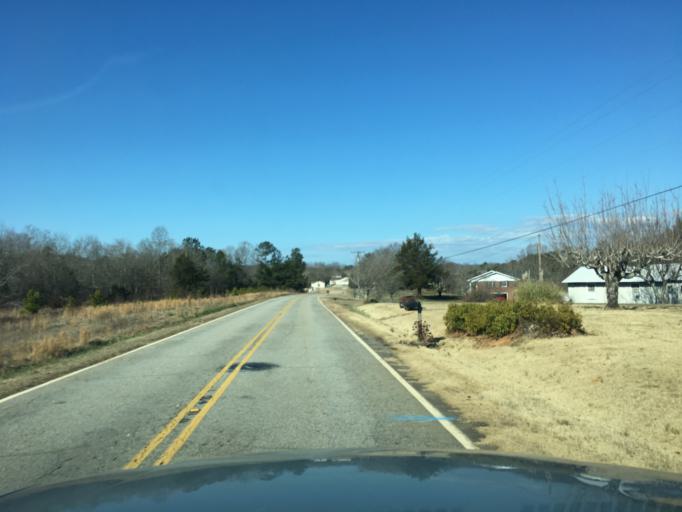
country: US
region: South Carolina
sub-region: Pickens County
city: Pickens
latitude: 34.8555
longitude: -82.7724
